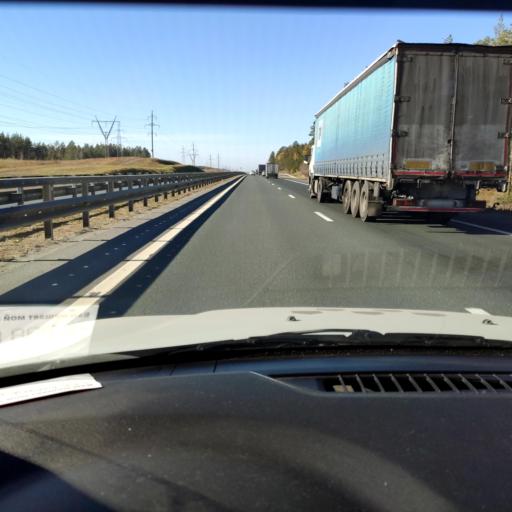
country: RU
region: Samara
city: Povolzhskiy
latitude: 53.5180
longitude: 49.7599
